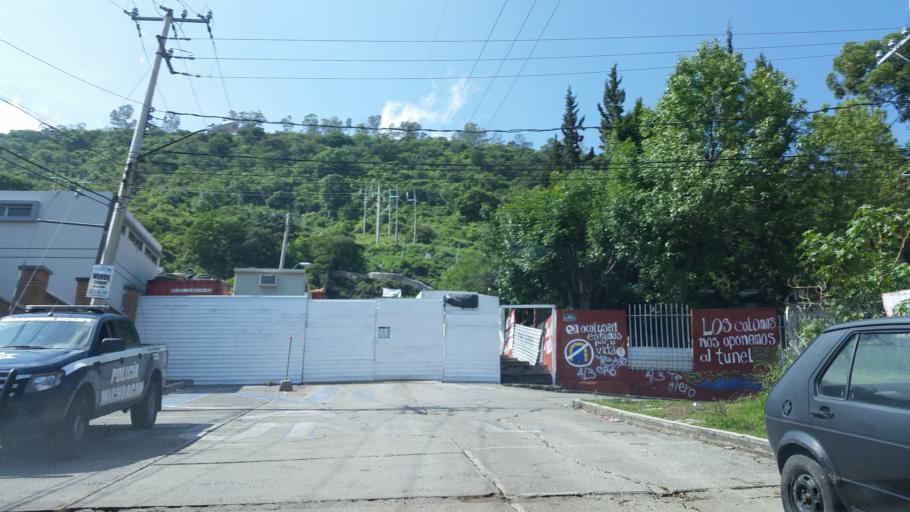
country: MX
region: Michoacan
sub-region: Morelia
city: Puerto de Buenavista (Lazaro Cardenas)
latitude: 19.6842
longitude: -101.1523
